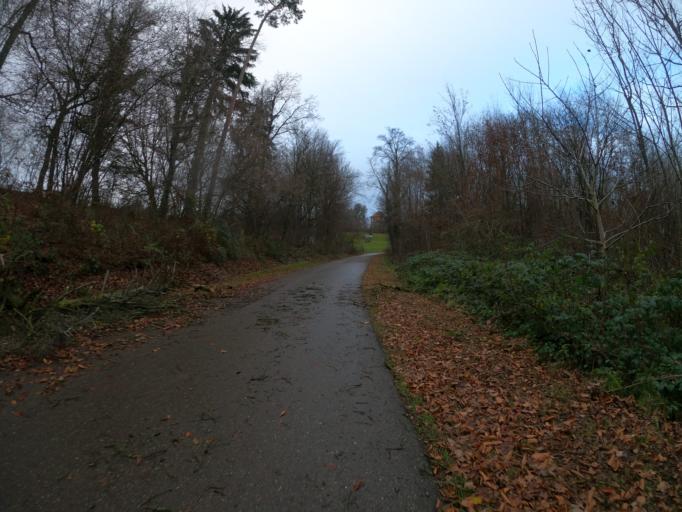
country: DE
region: Baden-Wuerttemberg
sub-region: Regierungsbezirk Stuttgart
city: Waschenbeuren
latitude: 48.7649
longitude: 9.7067
